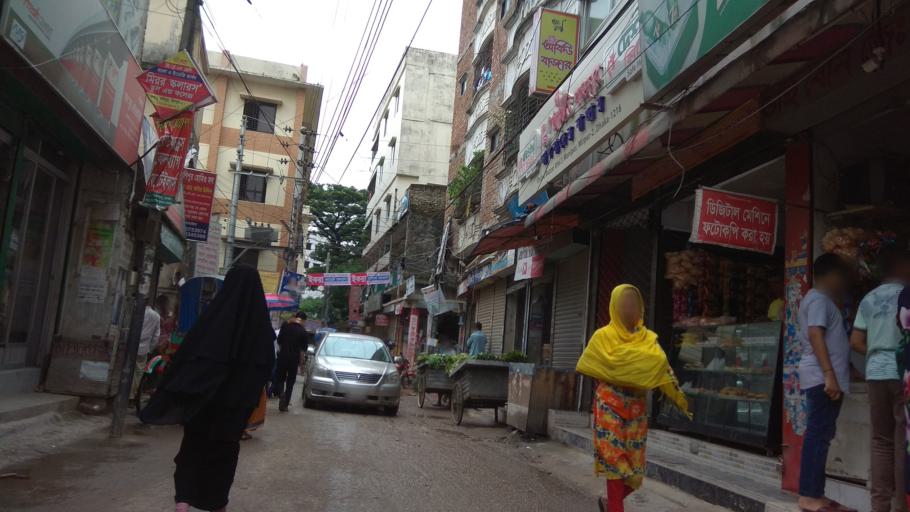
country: BD
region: Dhaka
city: Azimpur
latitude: 23.8000
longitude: 90.3657
